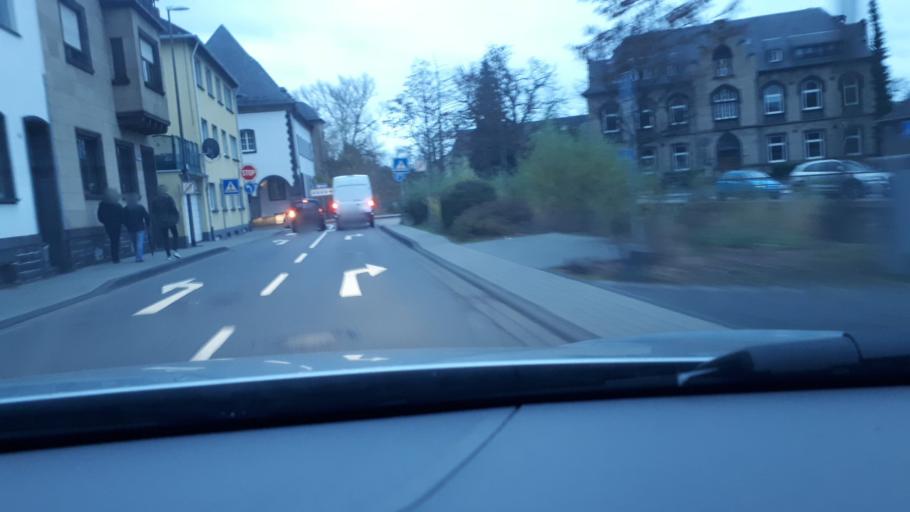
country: DE
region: Rheinland-Pfalz
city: Mayen
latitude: 50.3285
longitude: 7.2267
